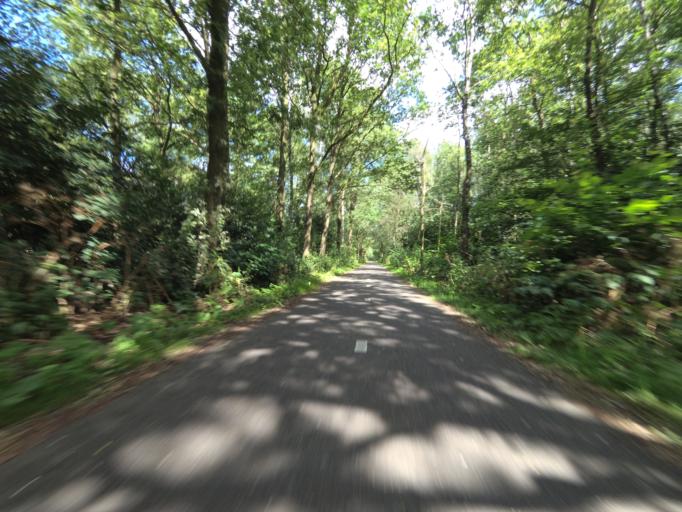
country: NL
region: Gelderland
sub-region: Gemeente Voorst
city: Twello
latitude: 52.1945
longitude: 6.0913
